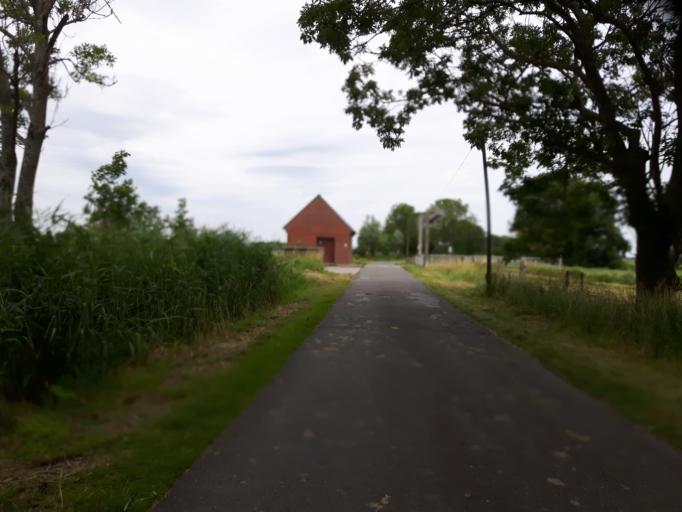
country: DE
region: Lower Saxony
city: Varel
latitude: 53.3615
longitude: 8.2051
